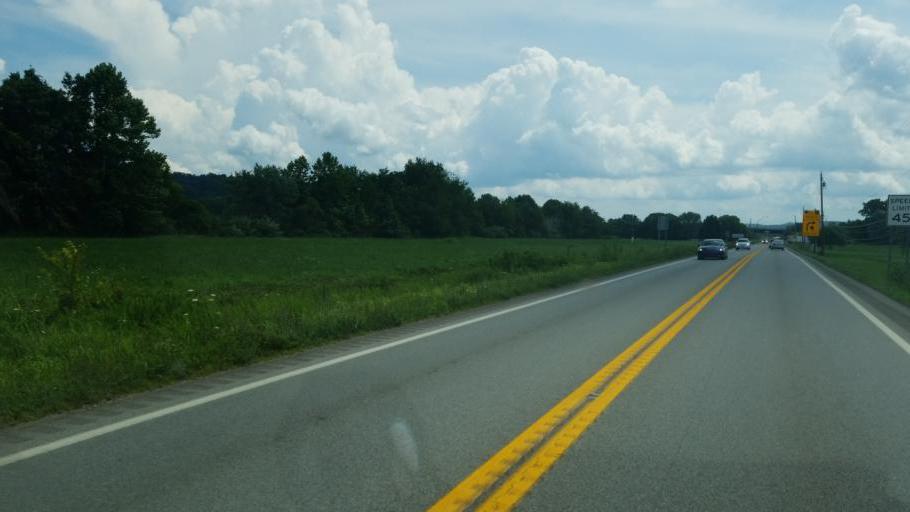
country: US
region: West Virginia
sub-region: Putnam County
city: Buffalo
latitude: 38.5879
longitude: -82.0045
